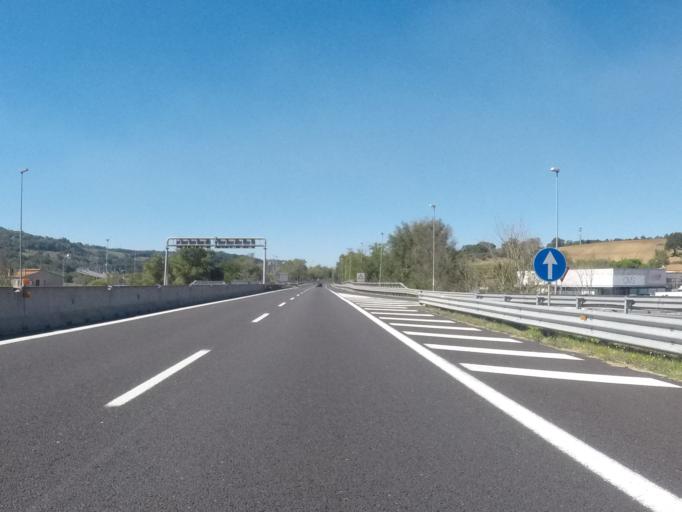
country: IT
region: Latium
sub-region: Provincia di Viterbo
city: Orte Scalo
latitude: 42.4509
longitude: 12.4064
